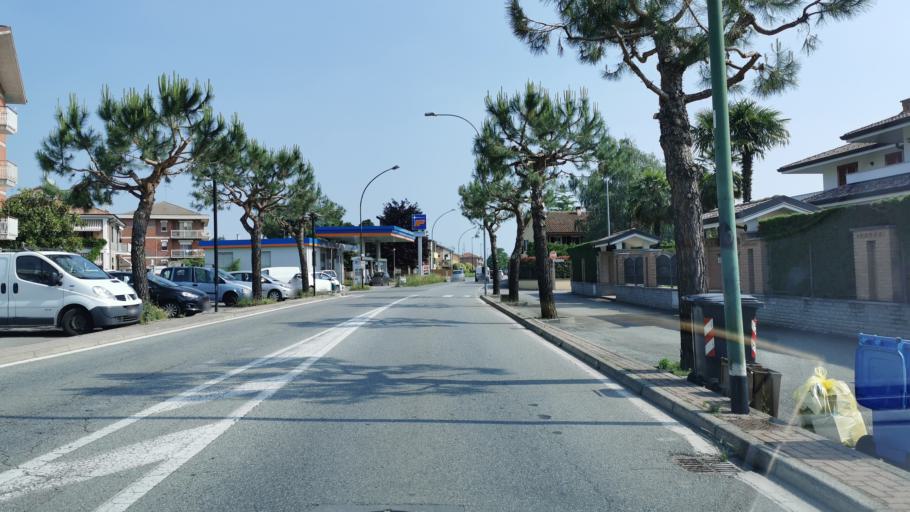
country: IT
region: Piedmont
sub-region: Provincia di Torino
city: Leini
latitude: 45.1891
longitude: 7.7198
